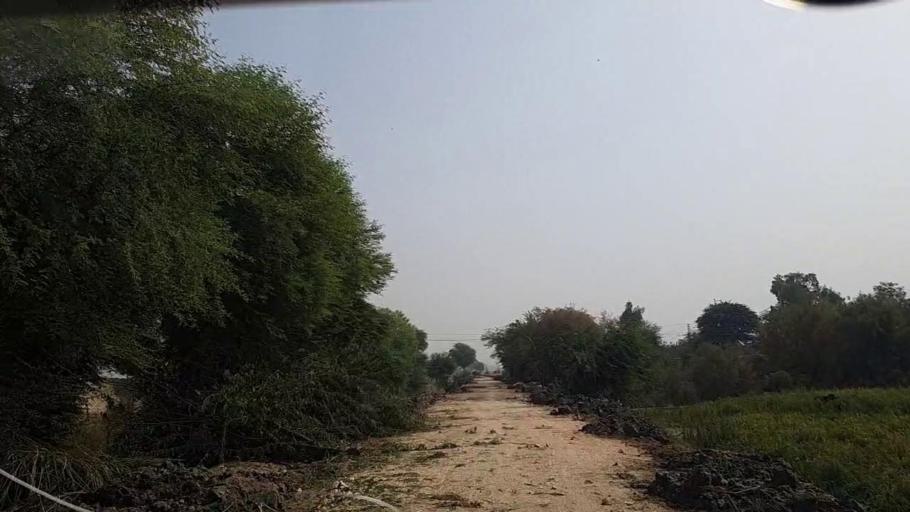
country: PK
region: Sindh
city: Shikarpur
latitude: 27.9197
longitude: 68.5826
